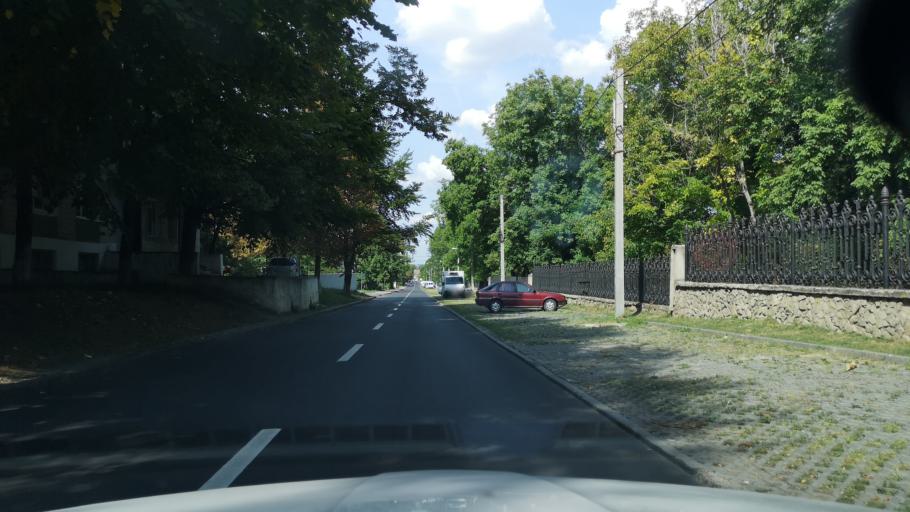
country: MD
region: Chisinau
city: Chisinau
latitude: 47.0243
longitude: 28.8091
